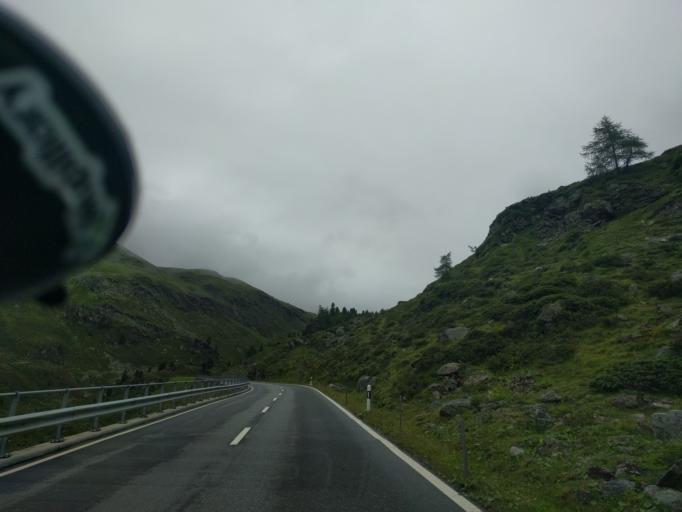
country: CH
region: Grisons
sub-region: Praettigau/Davos District
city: Davos
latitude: 46.7811
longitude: 9.9241
